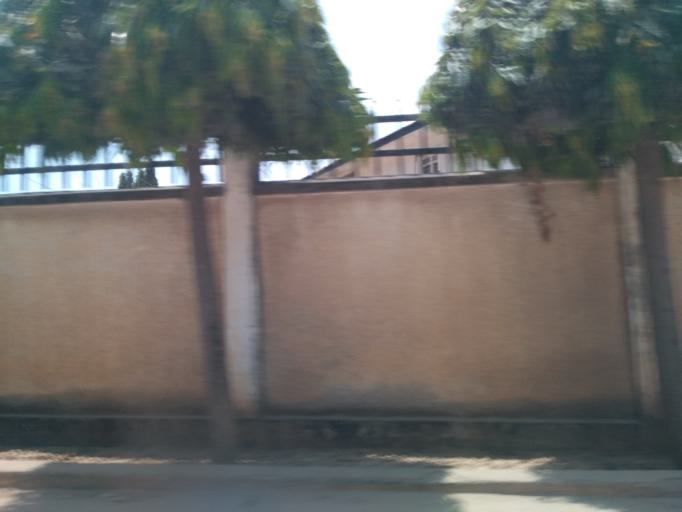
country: TZ
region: Dar es Salaam
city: Dar es Salaam
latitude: -6.8023
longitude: 39.2800
